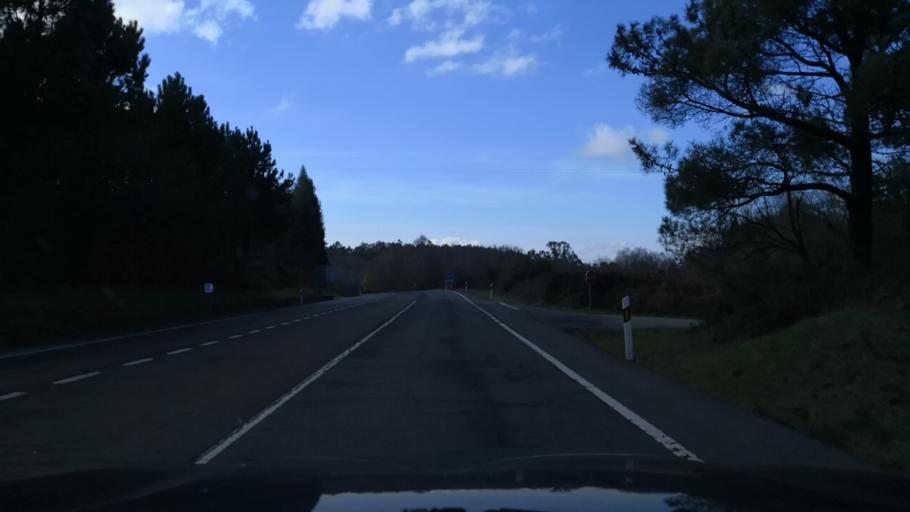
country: ES
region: Galicia
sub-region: Provincia da Coruna
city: Ribeira
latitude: 42.7104
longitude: -8.3538
